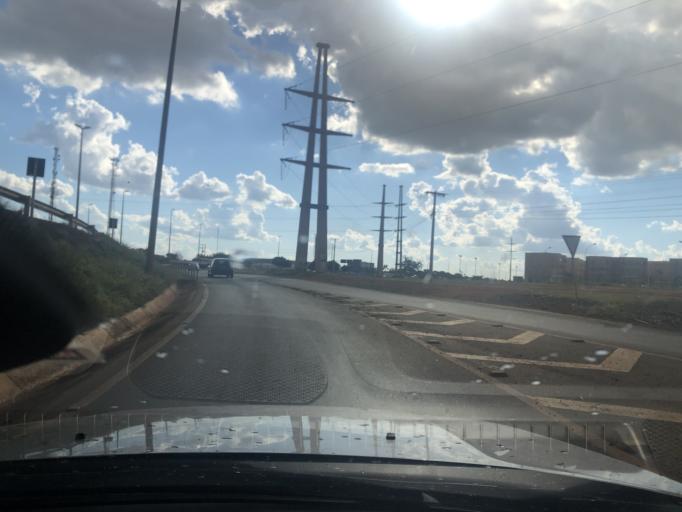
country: BR
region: Federal District
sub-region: Brasilia
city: Brasilia
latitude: -15.9648
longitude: -48.0202
